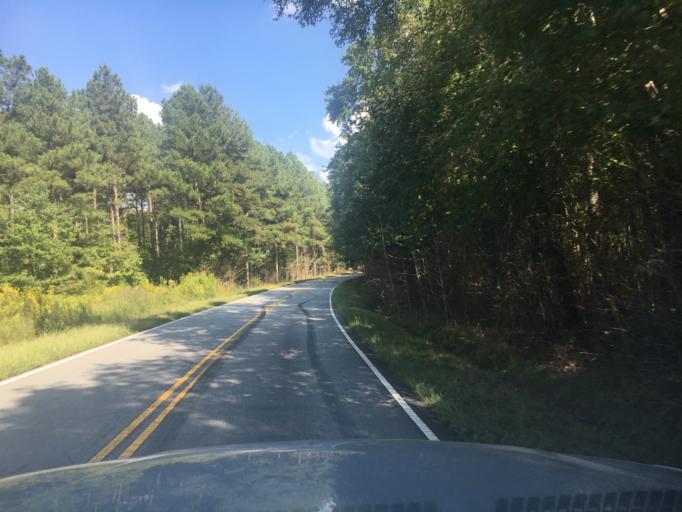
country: US
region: South Carolina
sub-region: Pickens County
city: Liberty
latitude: 34.7158
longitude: -82.6919
